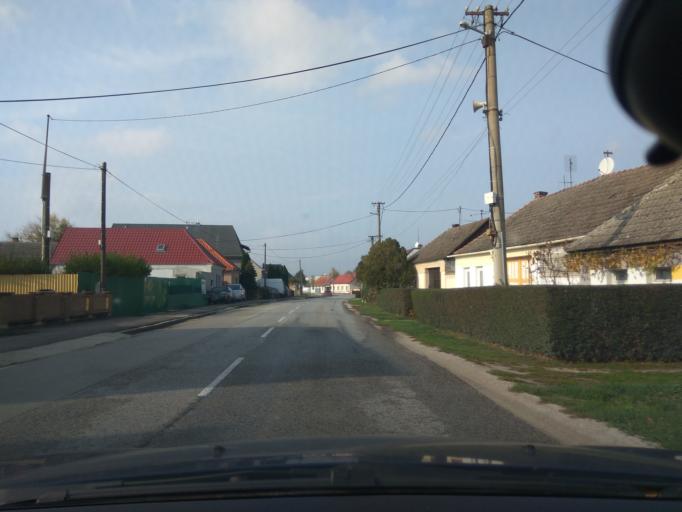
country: SK
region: Trnavsky
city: Vrbove
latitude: 48.6287
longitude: 17.7721
